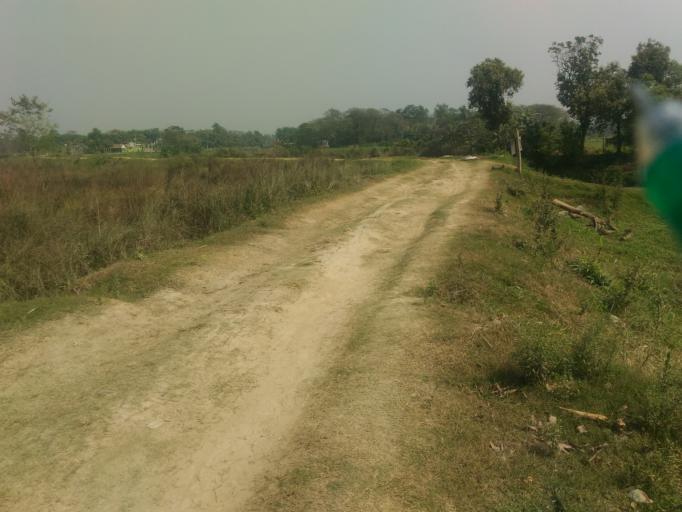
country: BD
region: Dhaka
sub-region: Dhaka
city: Dhaka
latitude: 23.6643
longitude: 90.4064
